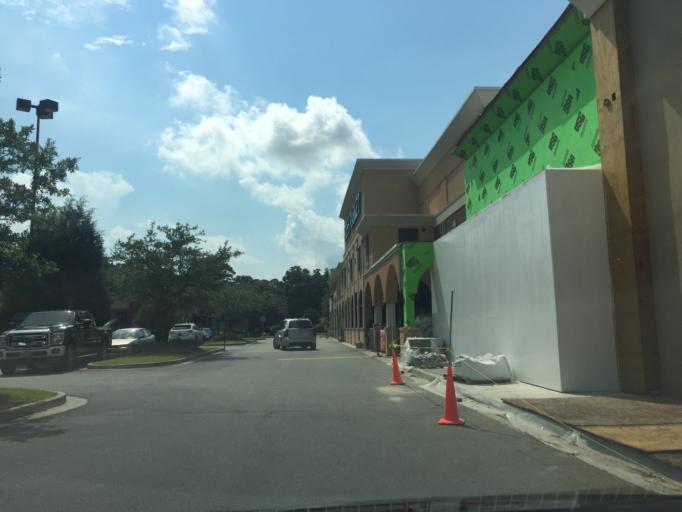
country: US
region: Georgia
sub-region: Chatham County
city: Savannah
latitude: 32.0245
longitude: -81.1109
